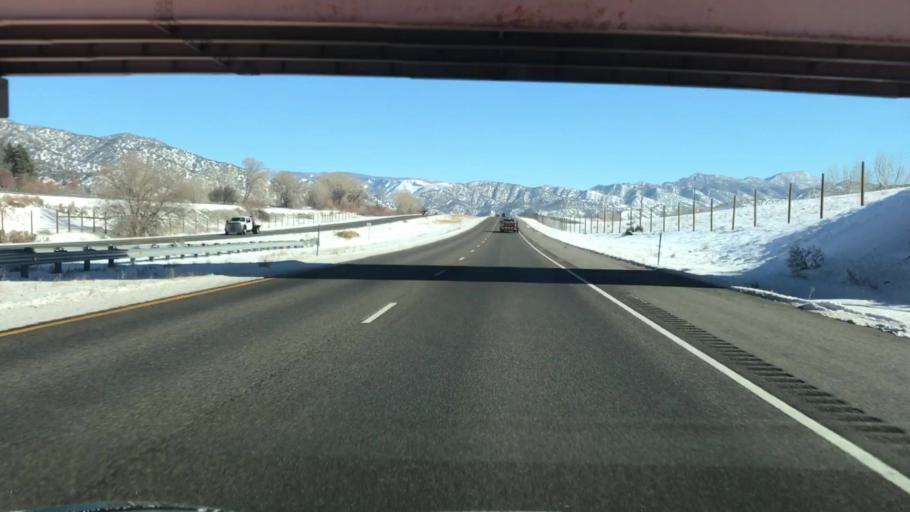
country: US
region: Colorado
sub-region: Garfield County
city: New Castle
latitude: 39.5513
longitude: -107.5937
